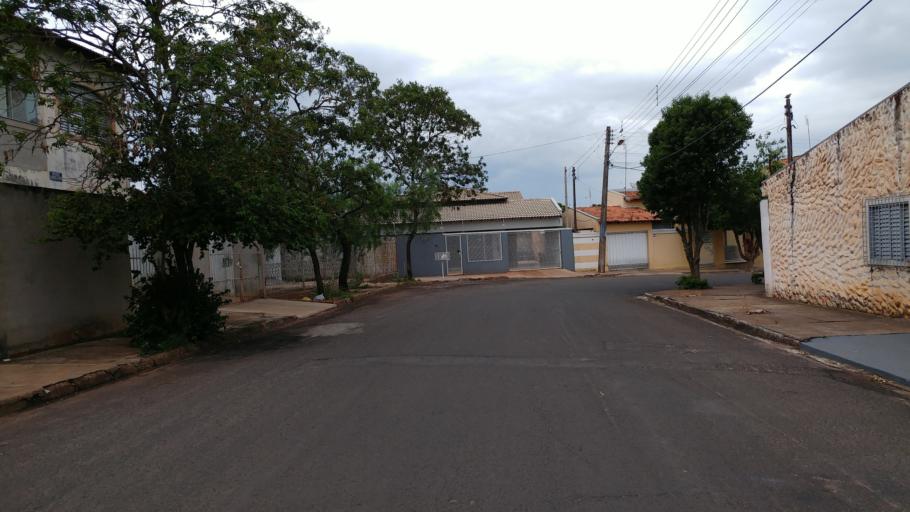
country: BR
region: Sao Paulo
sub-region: Paraguacu Paulista
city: Paraguacu Paulista
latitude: -22.4143
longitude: -50.5873
